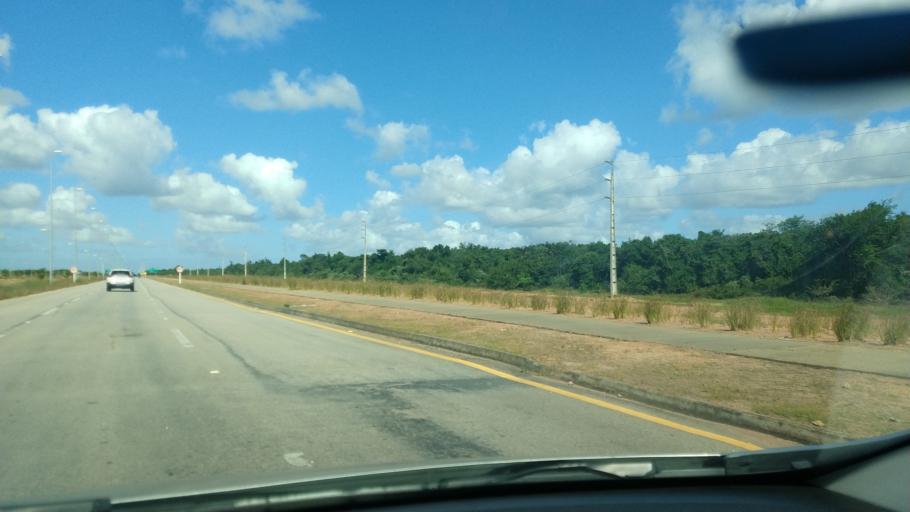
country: BR
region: Rio Grande do Norte
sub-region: Sao Goncalo Do Amarante
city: Sao Goncalo do Amarante
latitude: -5.7628
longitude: -35.3509
